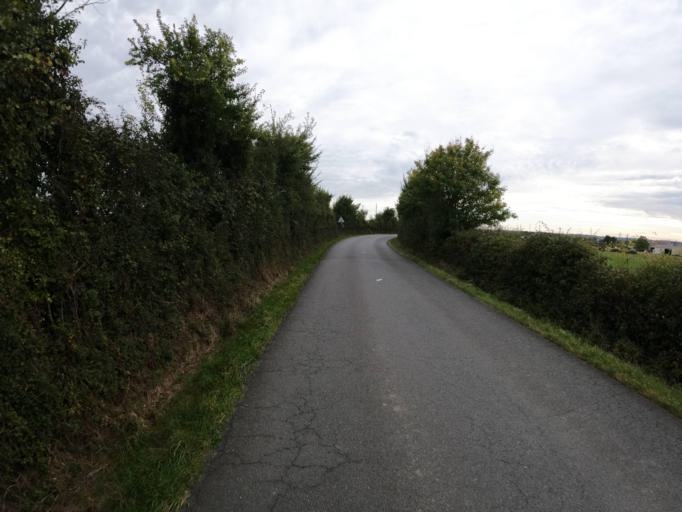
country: FR
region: Pays de la Loire
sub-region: Departement de Maine-et-Loire
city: Saint-Christophe-du-Bois
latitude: 47.0449
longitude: -0.9363
